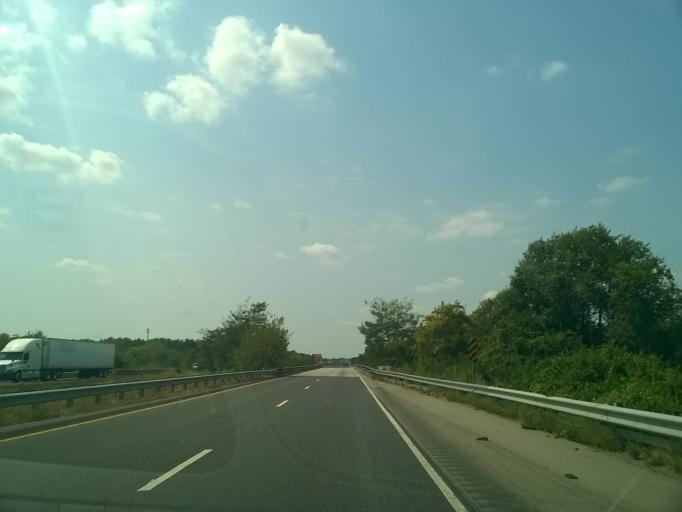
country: US
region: Indiana
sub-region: Vigo County
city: Terre Haute
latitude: 39.4312
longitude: -87.3807
